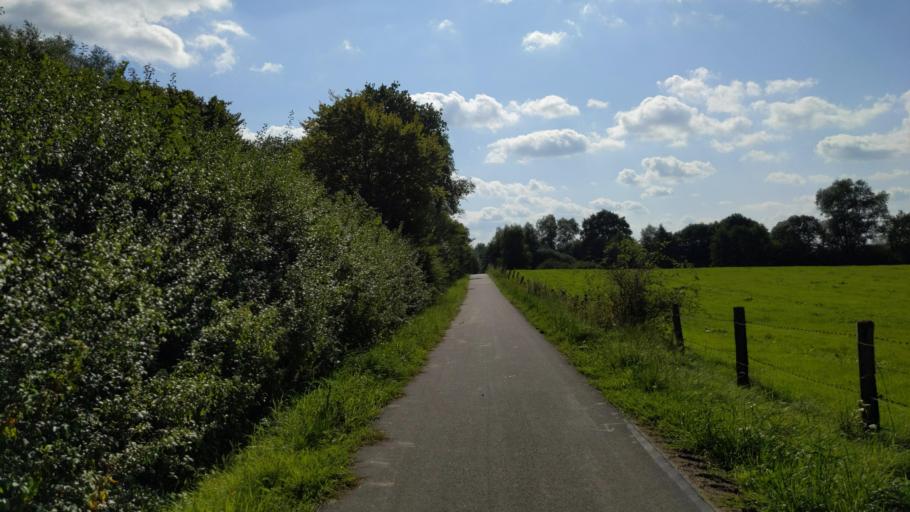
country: DE
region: Schleswig-Holstein
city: Schonwalde am Bungsberg
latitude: 54.1757
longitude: 10.7365
